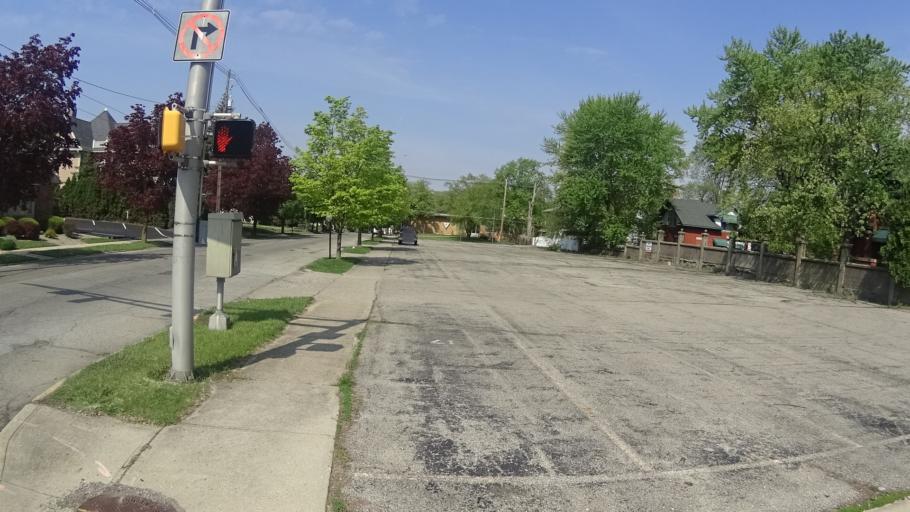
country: US
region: Indiana
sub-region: Madison County
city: Anderson
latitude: 40.1051
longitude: -85.6819
